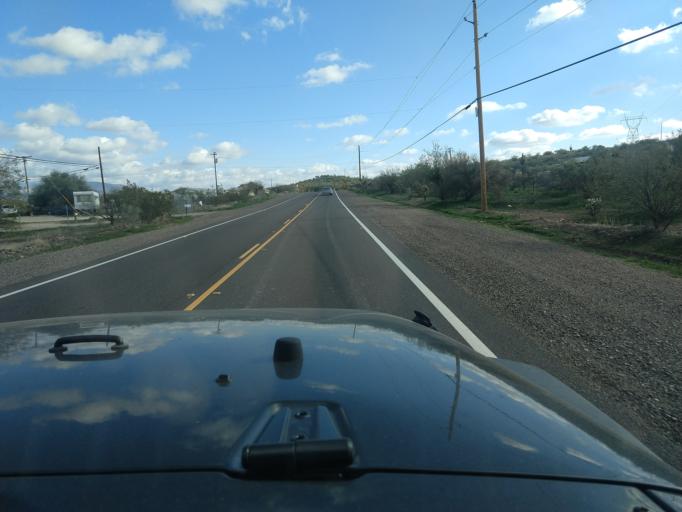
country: US
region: Arizona
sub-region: Maricopa County
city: New River
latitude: 33.9172
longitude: -112.1005
